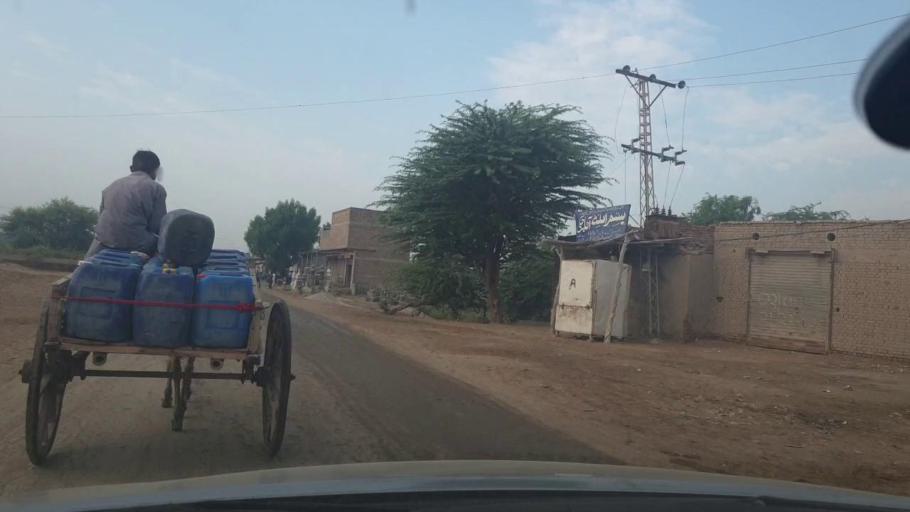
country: PK
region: Sindh
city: Jacobabad
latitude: 28.2779
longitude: 68.4239
